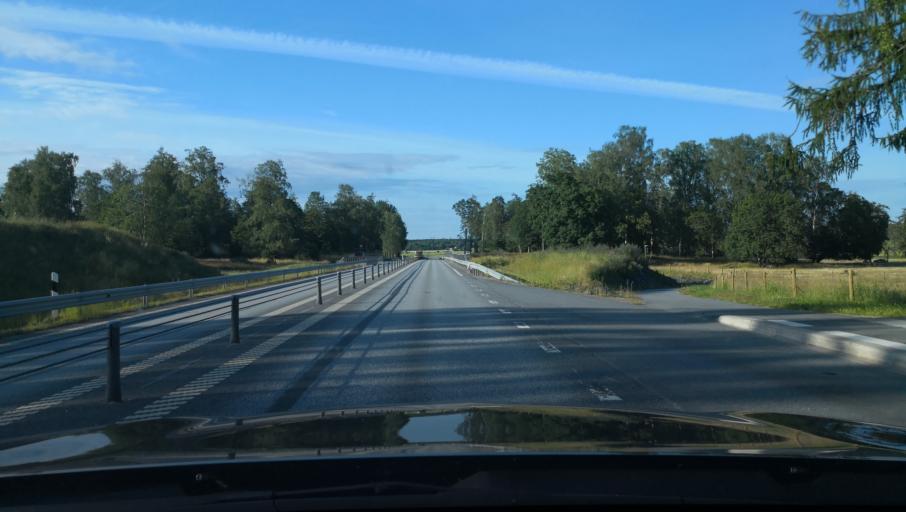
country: SE
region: Uppsala
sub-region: Osthammars Kommun
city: Osterbybruk
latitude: 60.0083
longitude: 17.9681
